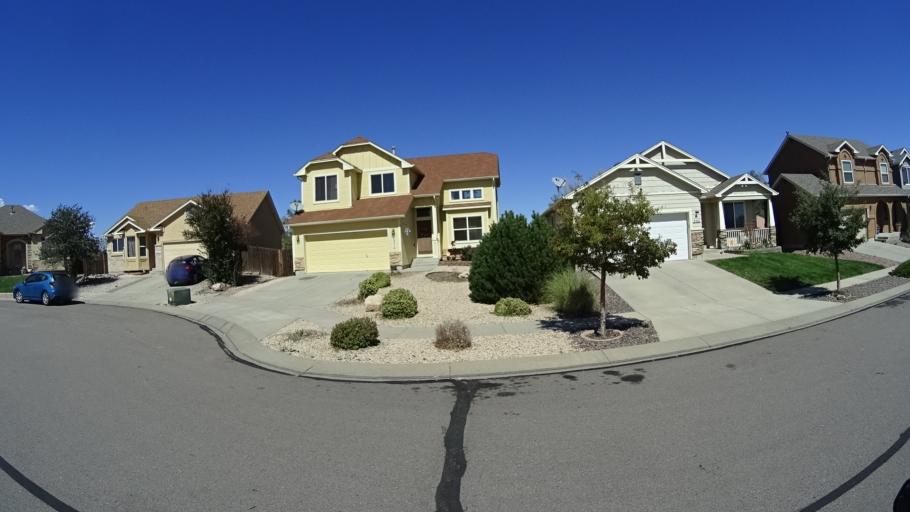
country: US
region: Colorado
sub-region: El Paso County
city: Security-Widefield
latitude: 38.7865
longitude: -104.7282
